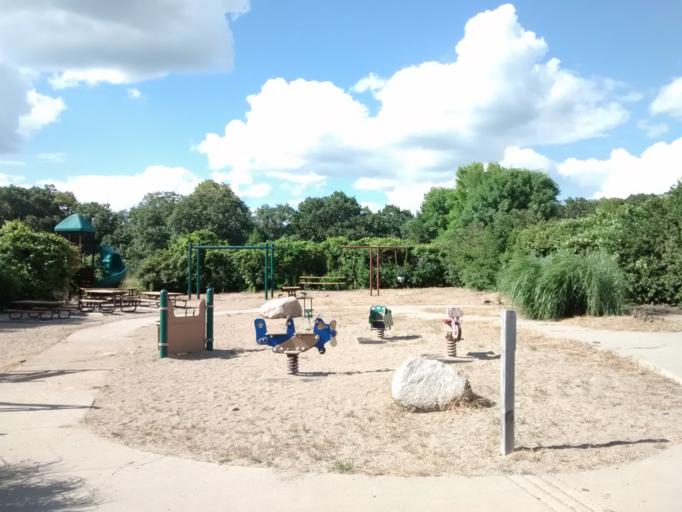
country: US
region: Iowa
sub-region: Dickinson County
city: Spirit Lake
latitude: 43.4120
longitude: -95.0732
